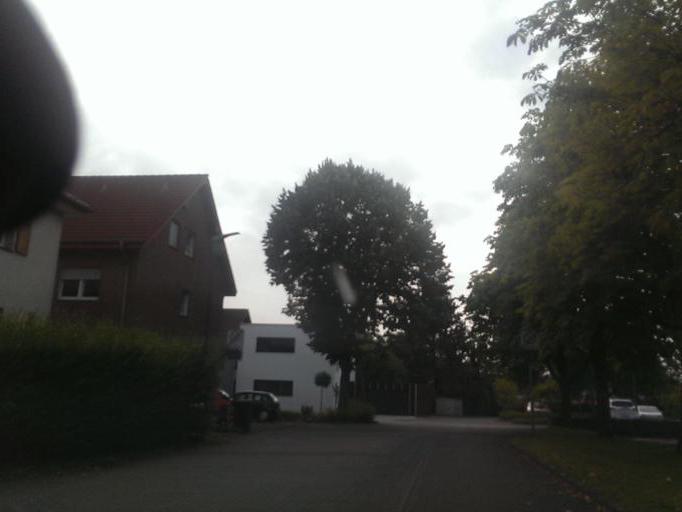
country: DE
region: North Rhine-Westphalia
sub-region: Regierungsbezirk Detmold
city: Delbruck
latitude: 51.7638
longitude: 8.5587
